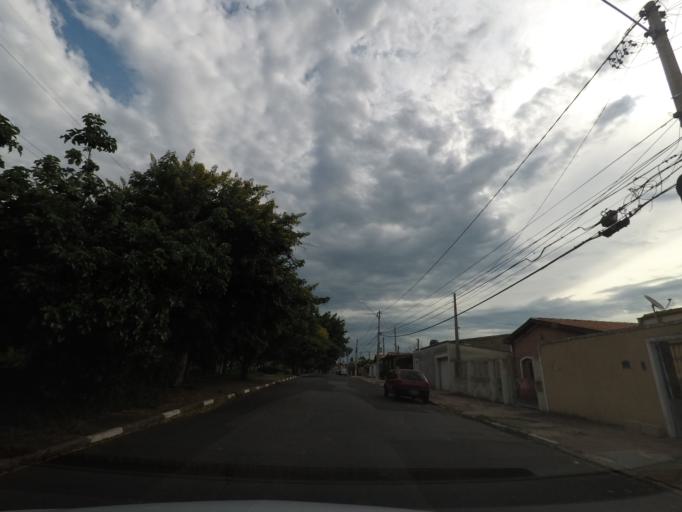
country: BR
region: Sao Paulo
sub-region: Campinas
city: Campinas
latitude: -22.8825
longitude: -47.1264
